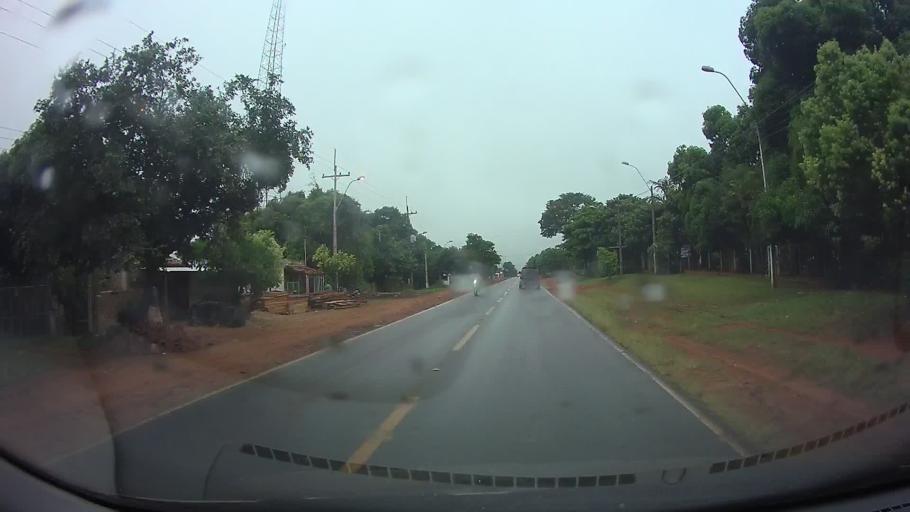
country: PY
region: Central
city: Ita
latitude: -25.4565
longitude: -57.3674
